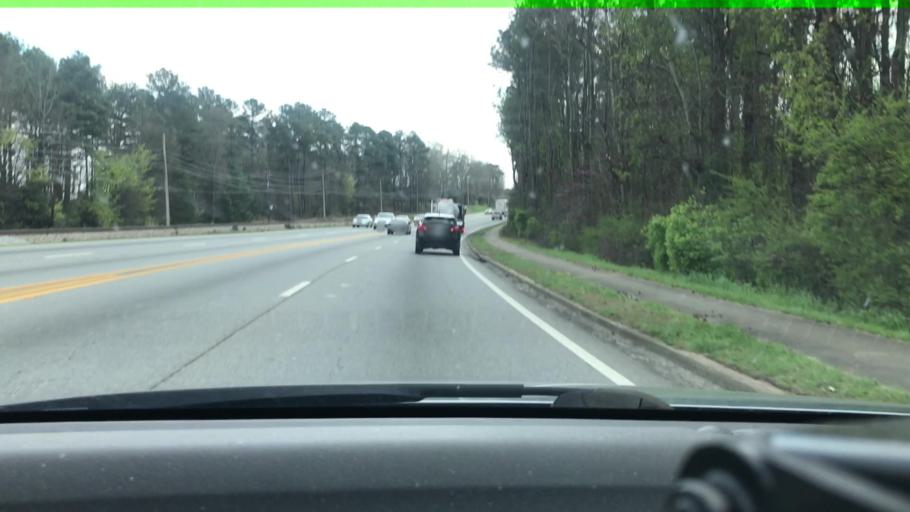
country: US
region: Georgia
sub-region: Clarke County
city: Country Club Estates
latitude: 33.9822
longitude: -83.4166
